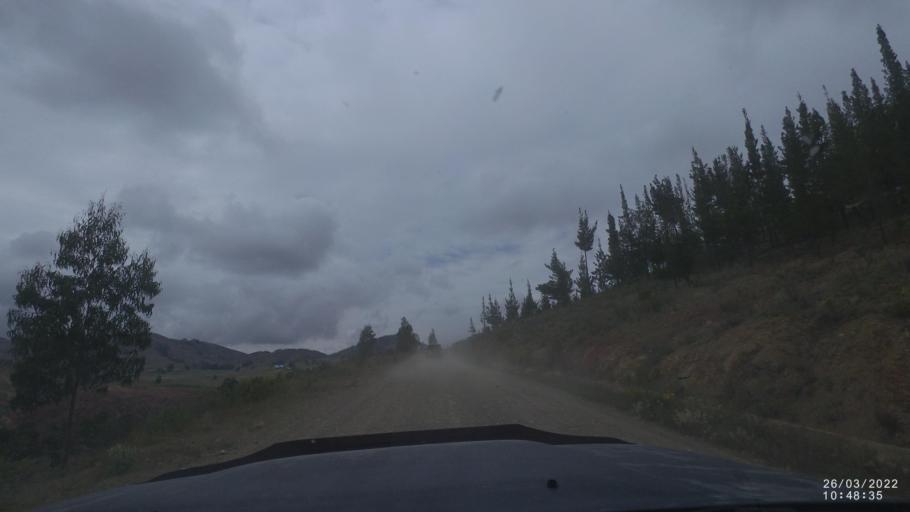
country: BO
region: Cochabamba
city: Tarata
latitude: -17.4964
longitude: -66.0433
